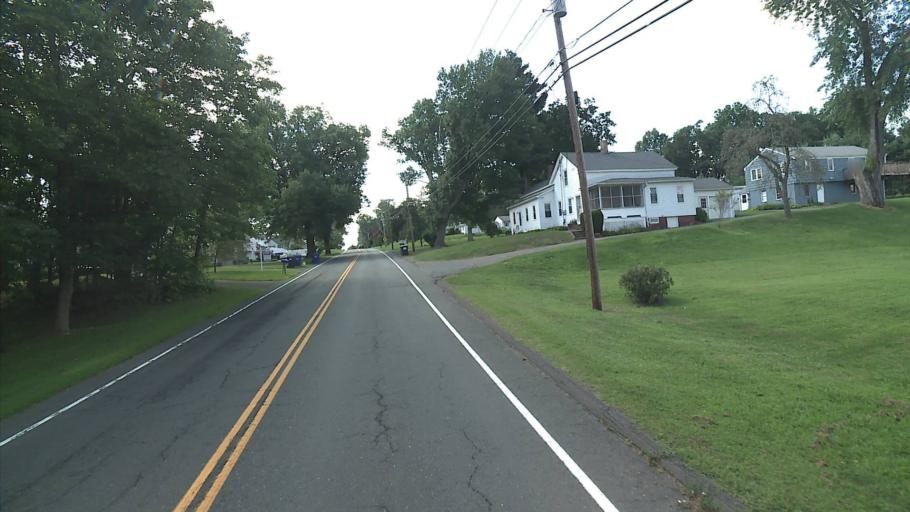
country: US
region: Connecticut
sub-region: Hartford County
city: Thompsonville
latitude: 41.9972
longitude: -72.6207
